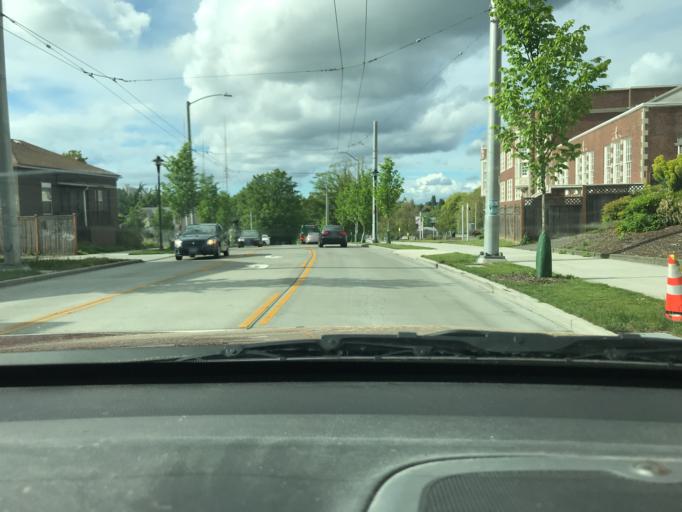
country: US
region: Washington
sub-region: King County
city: Seattle
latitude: 47.6045
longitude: -122.3024
